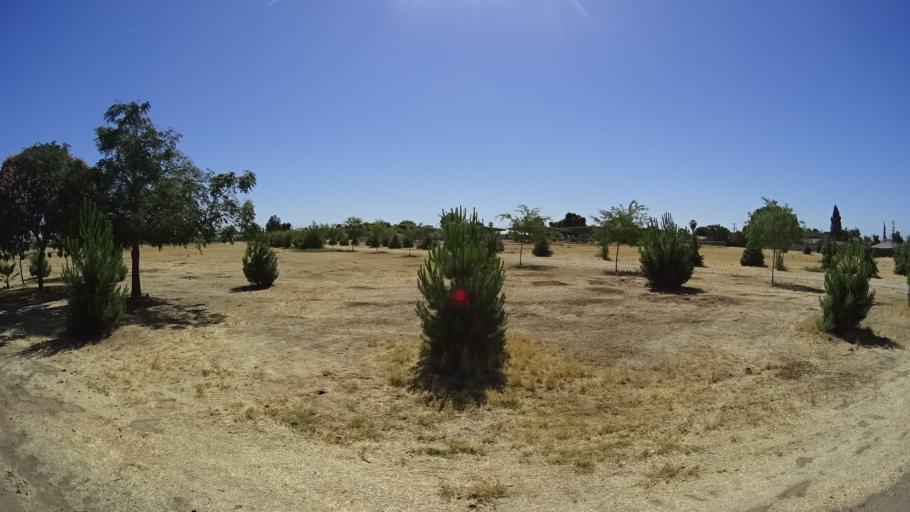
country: US
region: California
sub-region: Fresno County
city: Easton
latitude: 36.6949
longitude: -119.7976
